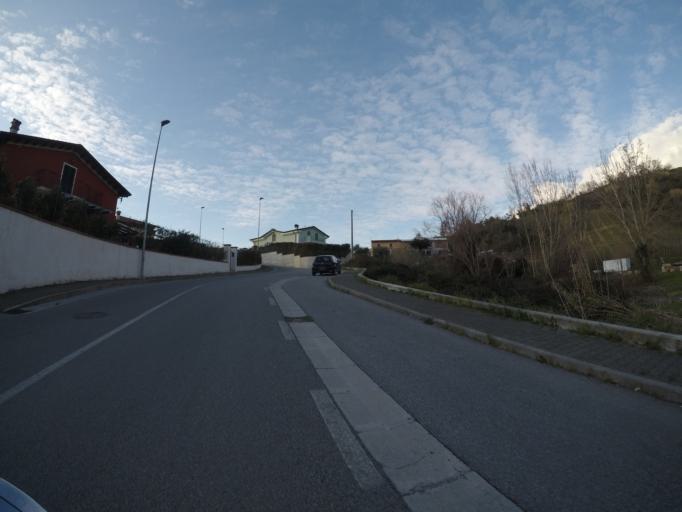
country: IT
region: Tuscany
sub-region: Provincia di Massa-Carrara
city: Carrara
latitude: 44.0614
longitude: 10.0873
